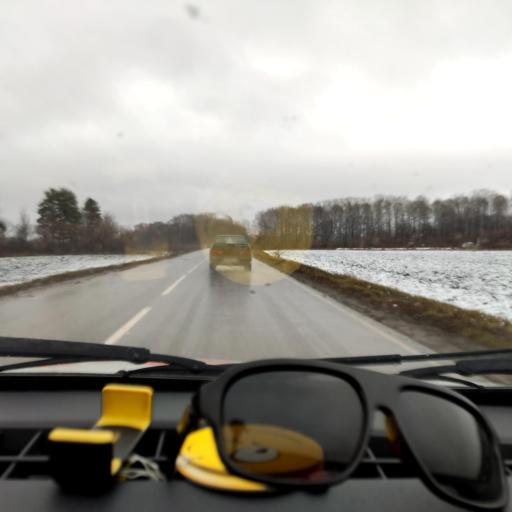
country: RU
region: Bashkortostan
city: Iglino
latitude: 54.8791
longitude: 56.5424
